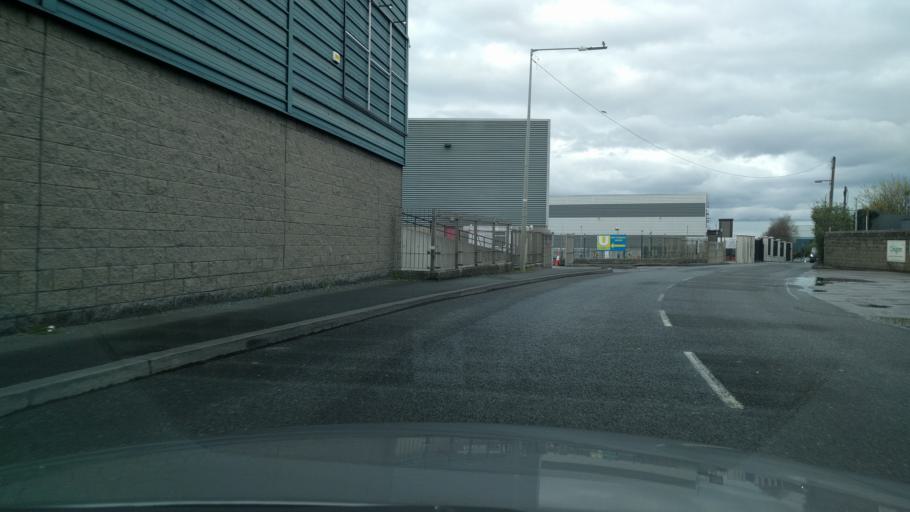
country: IE
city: Cherry Orchard
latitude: 53.3190
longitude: -6.3595
